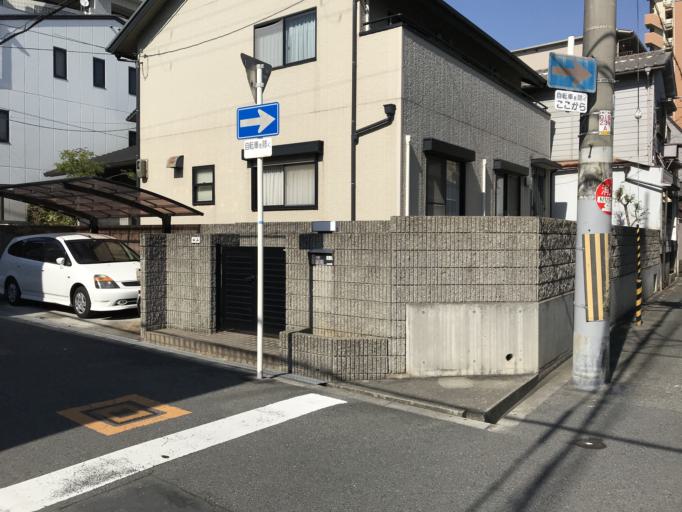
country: JP
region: Osaka
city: Osaka-shi
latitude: 34.6547
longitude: 135.5122
